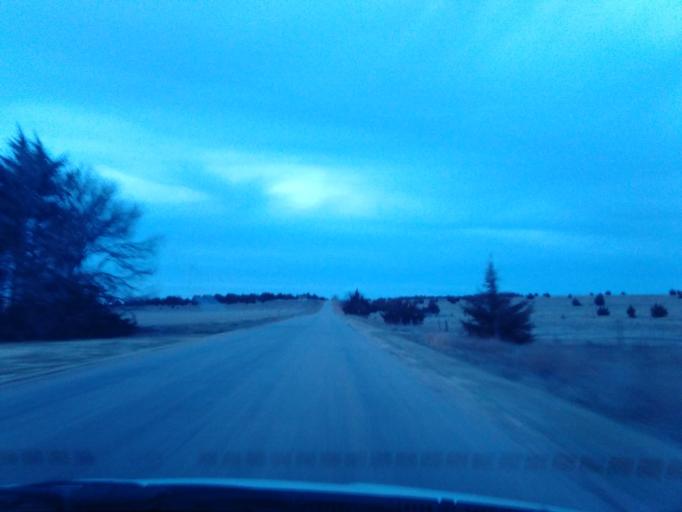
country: US
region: Nebraska
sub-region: Furnas County
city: Cambridge
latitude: 40.3658
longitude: -100.2121
